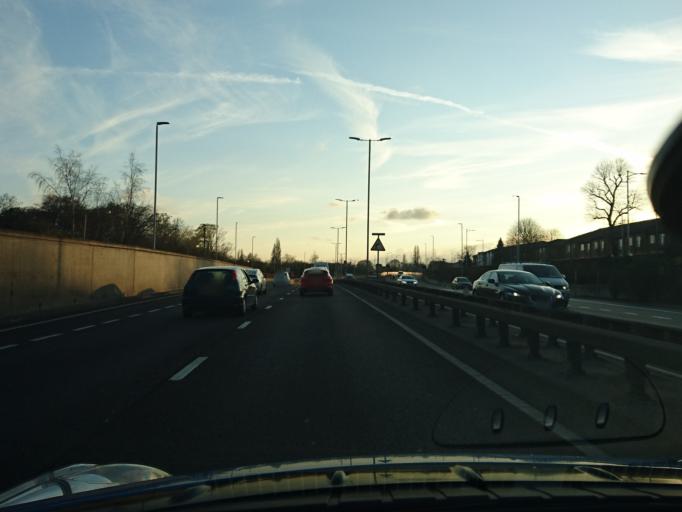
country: GB
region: England
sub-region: Greater London
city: Woodford Green
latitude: 51.5728
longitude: 0.0213
